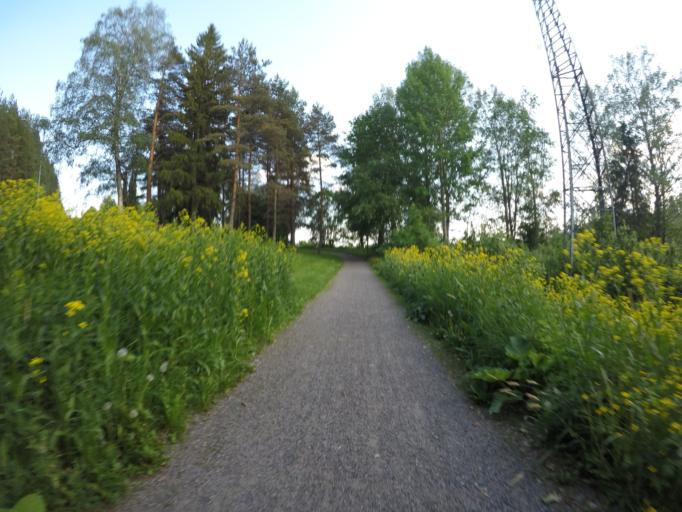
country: FI
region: Haeme
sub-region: Haemeenlinna
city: Haemeenlinna
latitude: 61.0142
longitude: 24.4552
